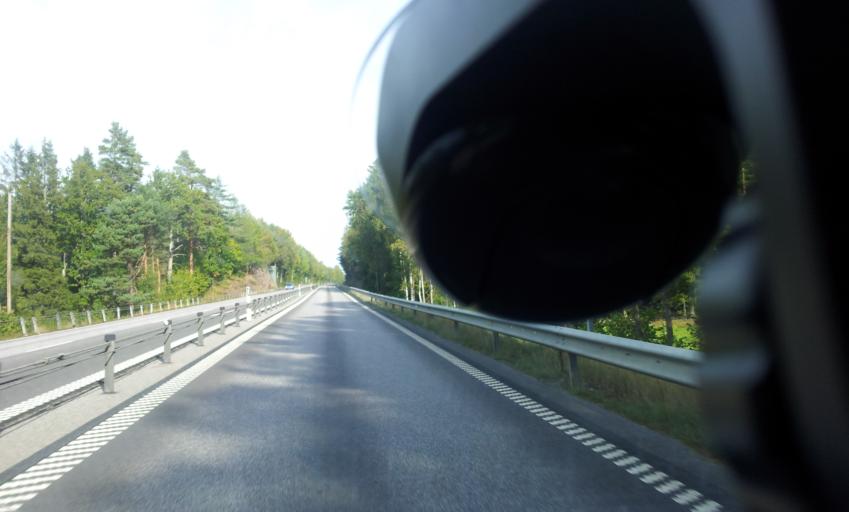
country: SE
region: Kalmar
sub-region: Oskarshamns Kommun
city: Oskarshamn
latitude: 57.3152
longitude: 16.4652
